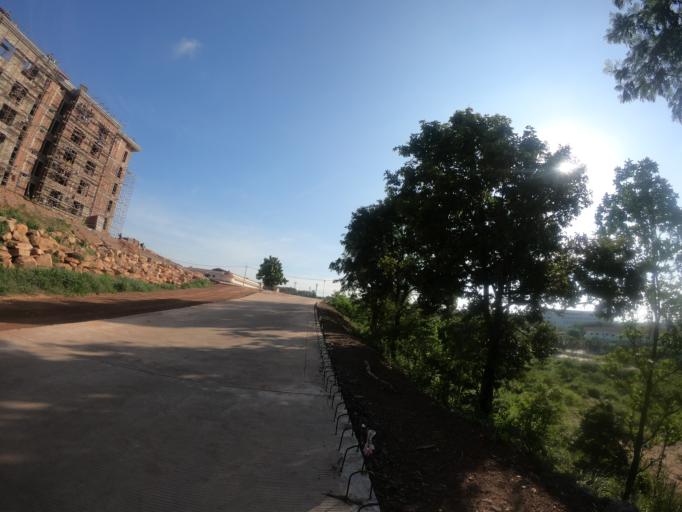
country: TH
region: Surin
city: Kap Choeng
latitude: 14.4318
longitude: 103.6976
